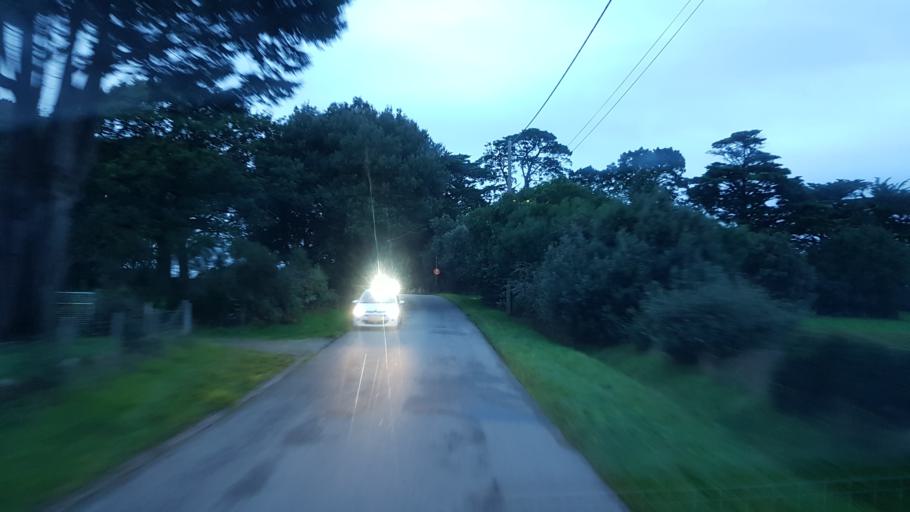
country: FR
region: Brittany
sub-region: Departement du Morbihan
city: Sarzeau
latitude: 47.5379
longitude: -2.8011
